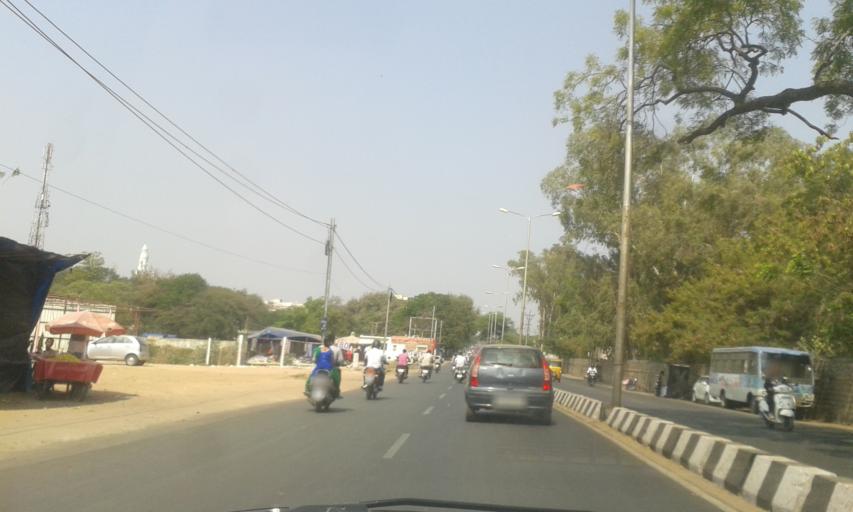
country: IN
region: Telangana
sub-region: Rangareddi
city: Secunderabad
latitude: 17.4953
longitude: 78.5129
